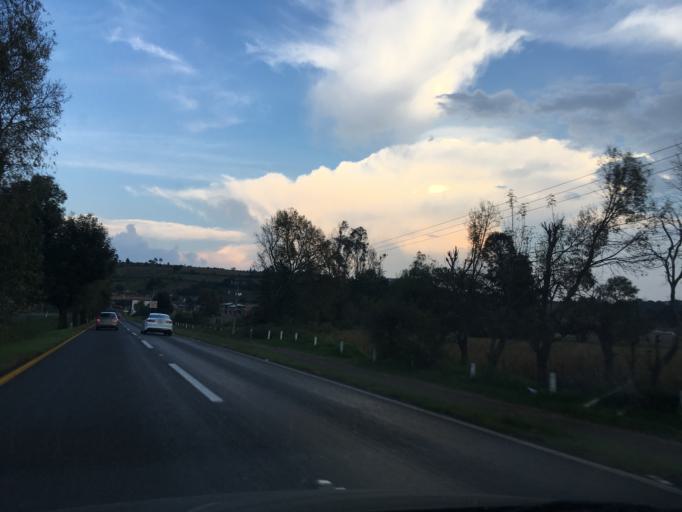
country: MX
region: Michoacan
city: Huiramba
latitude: 19.5485
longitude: -101.4366
